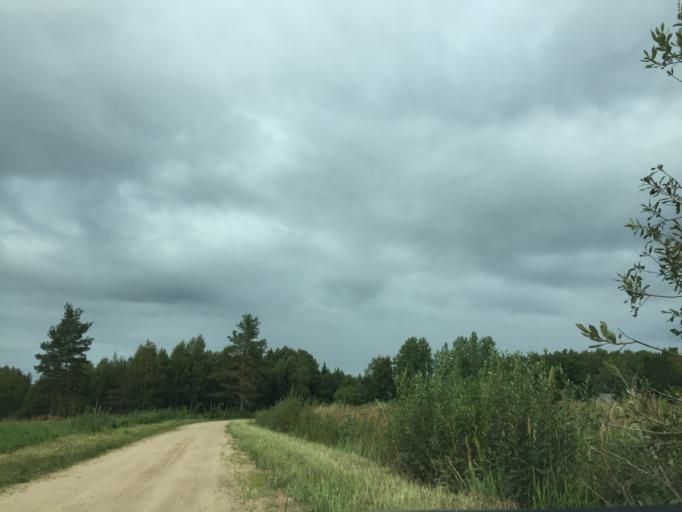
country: LV
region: Pargaujas
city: Stalbe
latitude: 57.5047
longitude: 24.9181
